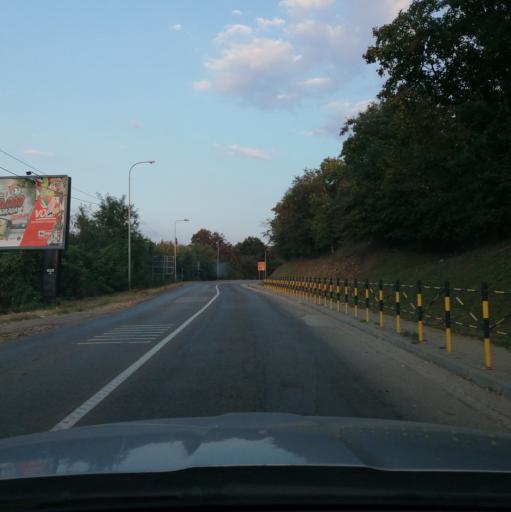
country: RS
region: Central Serbia
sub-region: Raski Okrug
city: Kraljevo
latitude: 43.7373
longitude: 20.6712
